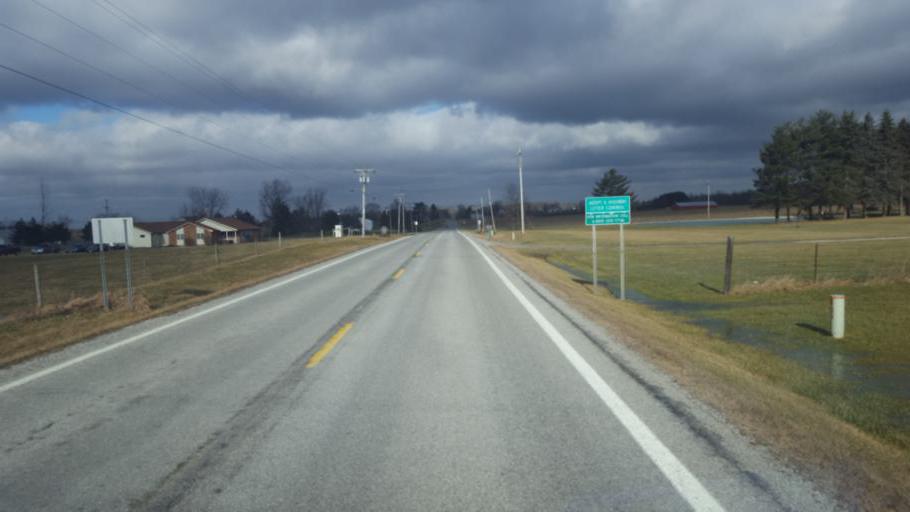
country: US
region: Ohio
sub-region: Morrow County
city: Mount Gilead
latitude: 40.5143
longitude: -82.8171
